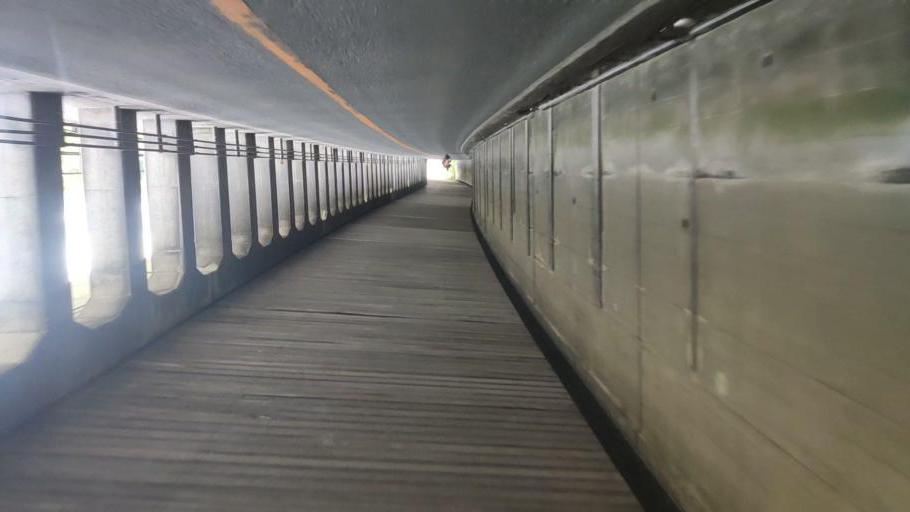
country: JP
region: Gifu
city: Takayama
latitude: 36.1764
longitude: 137.2493
